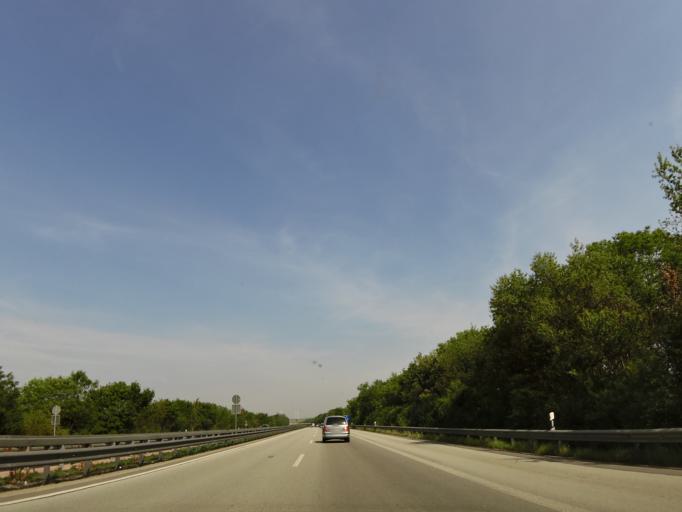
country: DE
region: Rheinland-Pfalz
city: Gundheim
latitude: 49.6866
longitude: 8.2433
